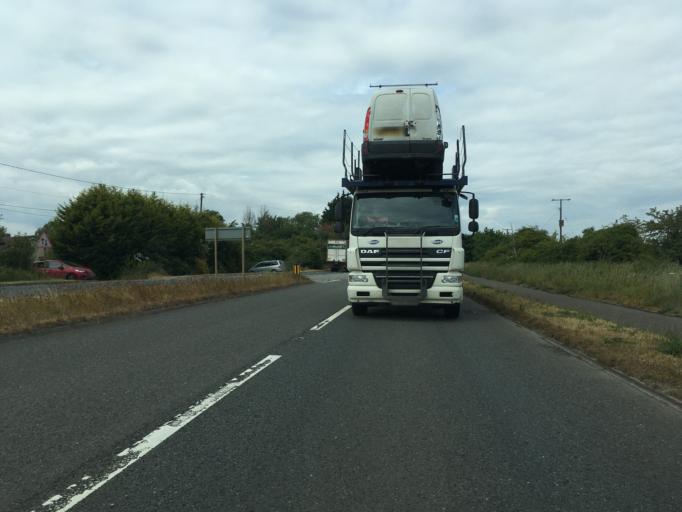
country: GB
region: England
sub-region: South Gloucestershire
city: Severn Beach
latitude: 51.5791
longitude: -2.6408
